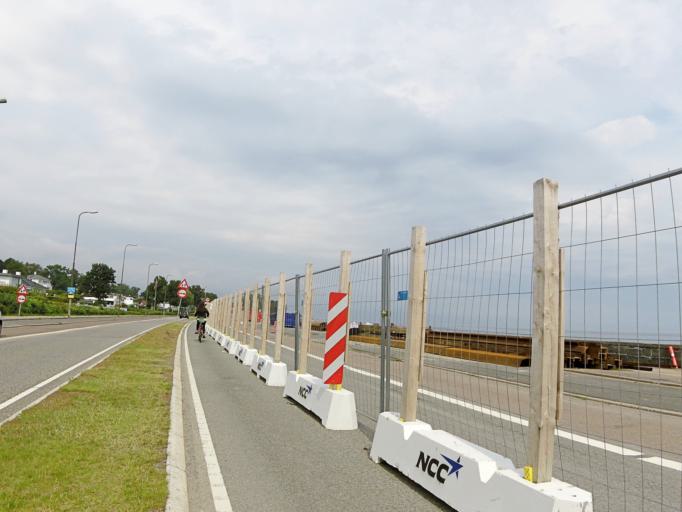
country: DK
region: Capital Region
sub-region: Gentofte Kommune
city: Charlottenlund
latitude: 55.7659
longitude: 12.5972
